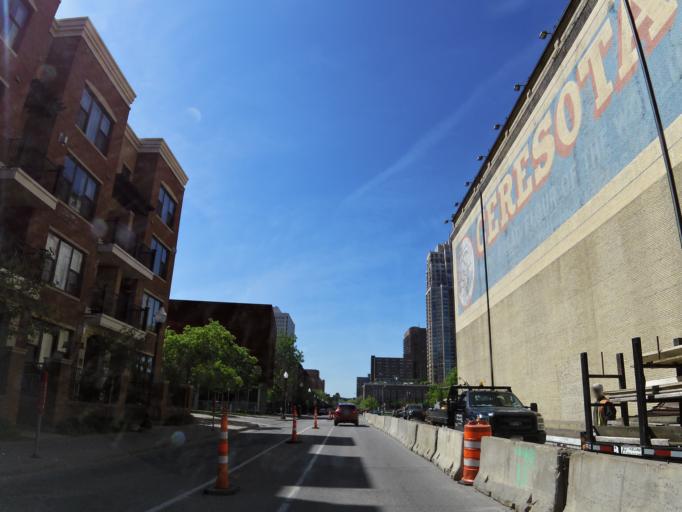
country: US
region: Minnesota
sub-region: Hennepin County
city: Minneapolis
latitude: 44.9795
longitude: -93.2595
